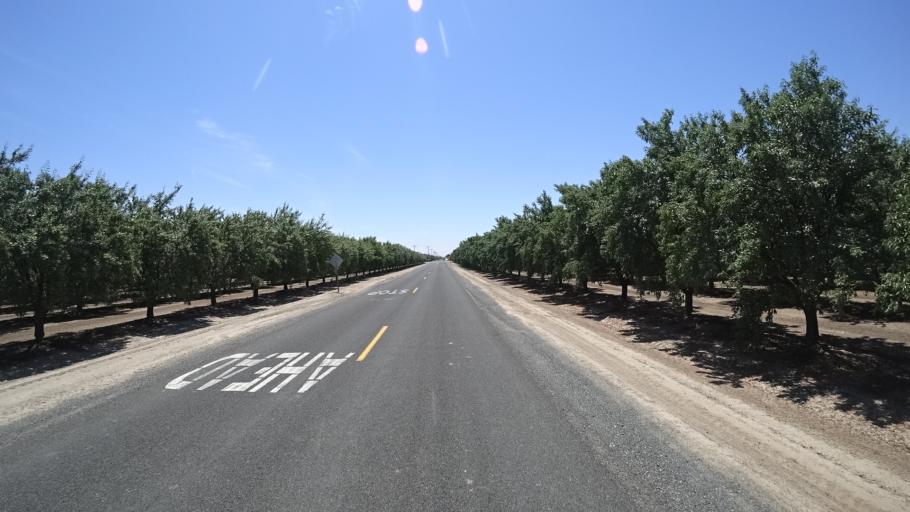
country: US
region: California
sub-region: Kings County
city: Armona
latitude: 36.3304
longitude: -119.7180
